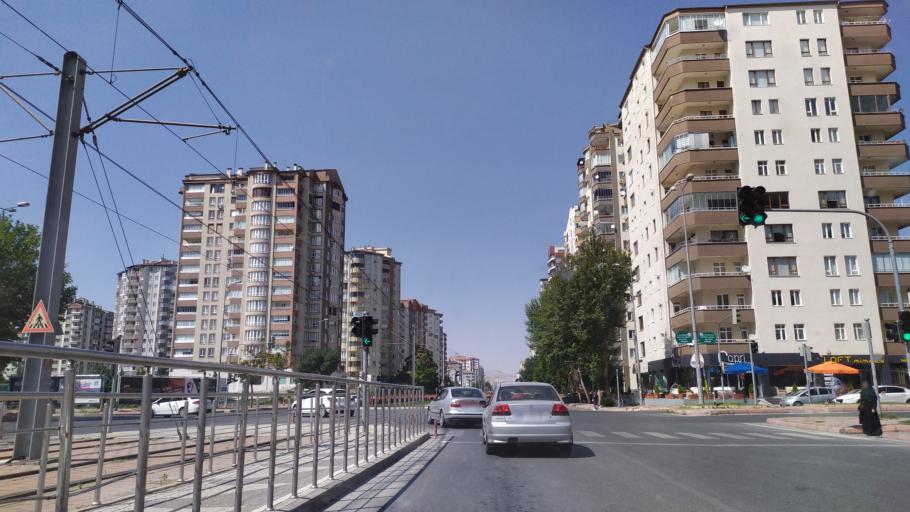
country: TR
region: Kayseri
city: Kayseri
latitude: 38.7276
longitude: 35.5259
